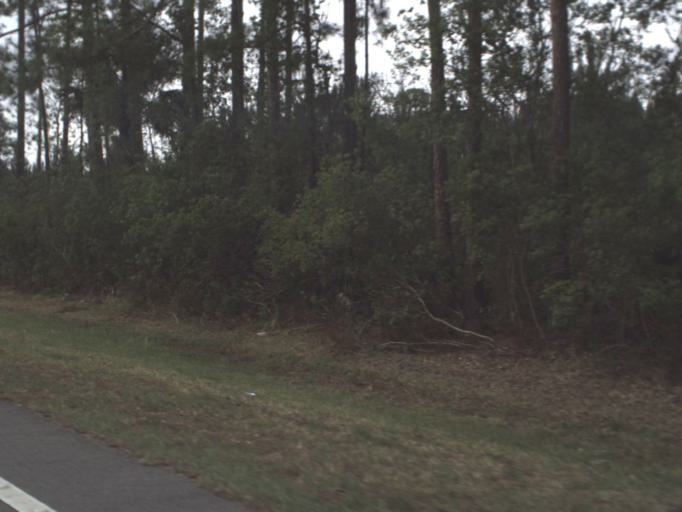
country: US
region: Florida
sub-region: Flagler County
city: Bunnell
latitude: 29.4734
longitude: -81.3263
